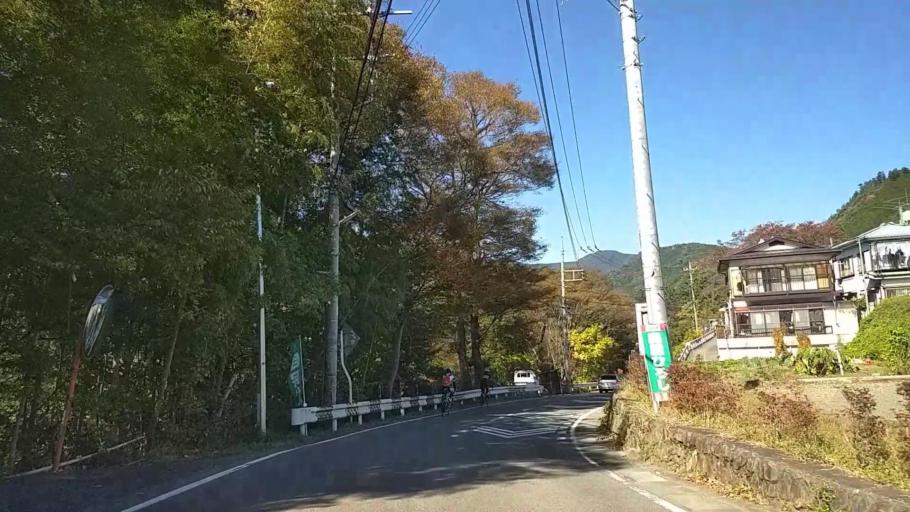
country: JP
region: Yamanashi
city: Uenohara
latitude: 35.6400
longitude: 139.1028
